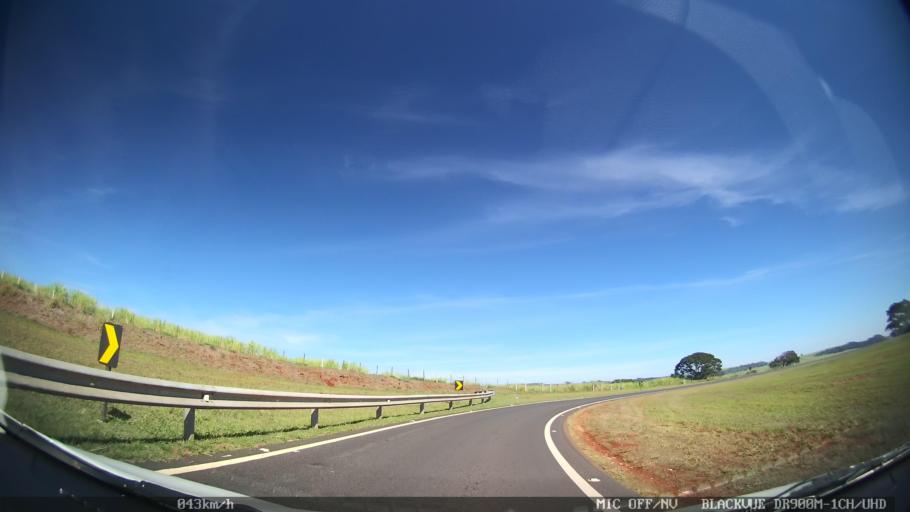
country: BR
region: Sao Paulo
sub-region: Santa Rita Do Passa Quatro
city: Santa Rita do Passa Quatro
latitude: -21.7569
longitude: -47.5634
